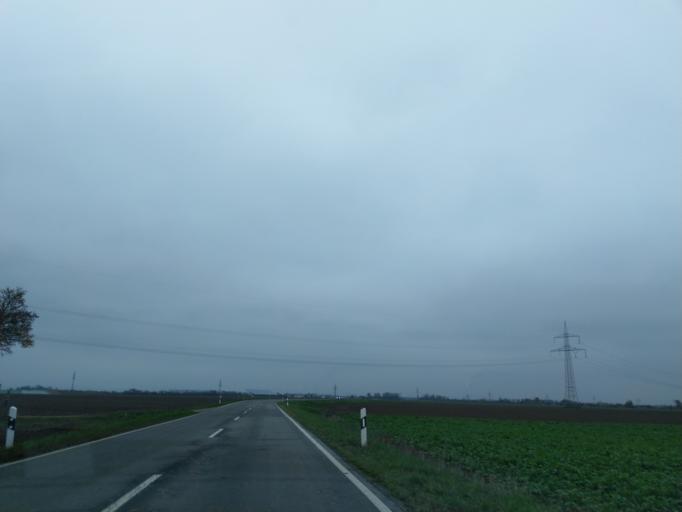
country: DE
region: Bavaria
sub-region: Lower Bavaria
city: Otzing
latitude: 48.7813
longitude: 12.8021
